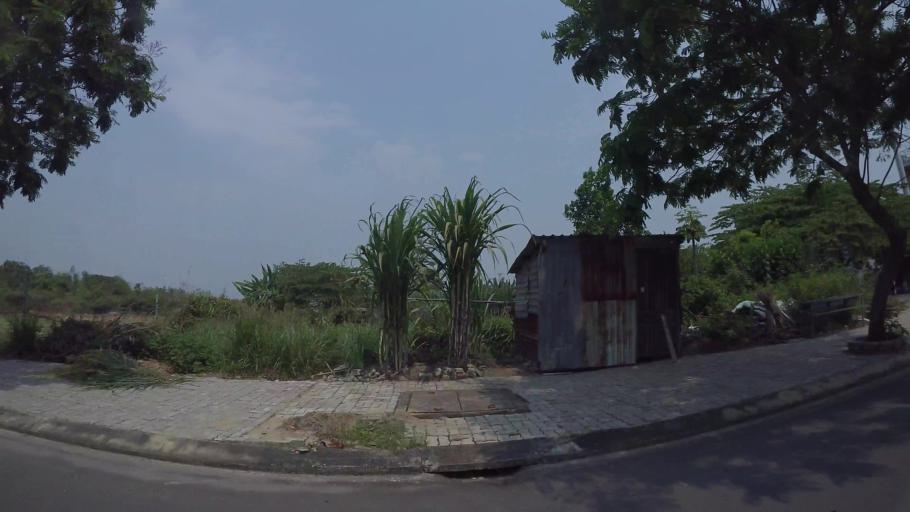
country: VN
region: Da Nang
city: Cam Le
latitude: 16.0065
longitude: 108.2126
